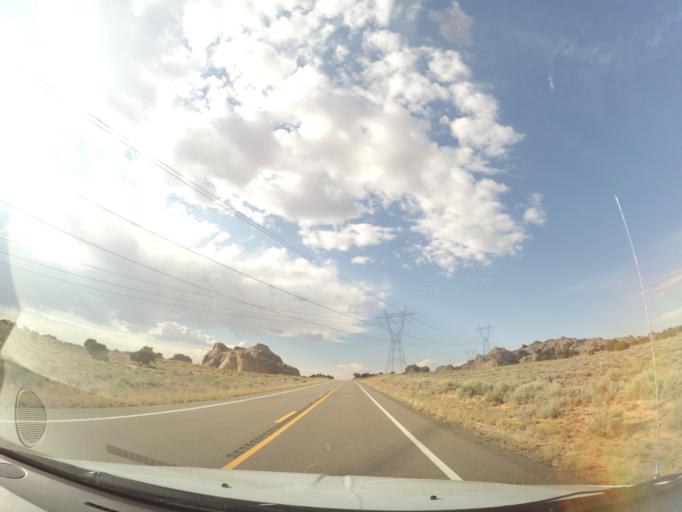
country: US
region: Arizona
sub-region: Coconino County
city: LeChee
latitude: 36.6060
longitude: -111.4310
